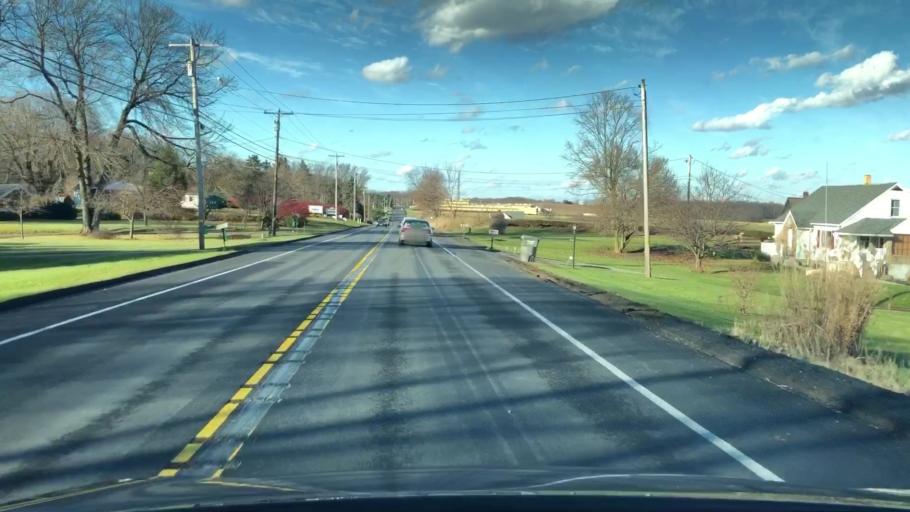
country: US
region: Pennsylvania
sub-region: Butler County
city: Saxonburg
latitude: 40.7747
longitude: -79.7951
